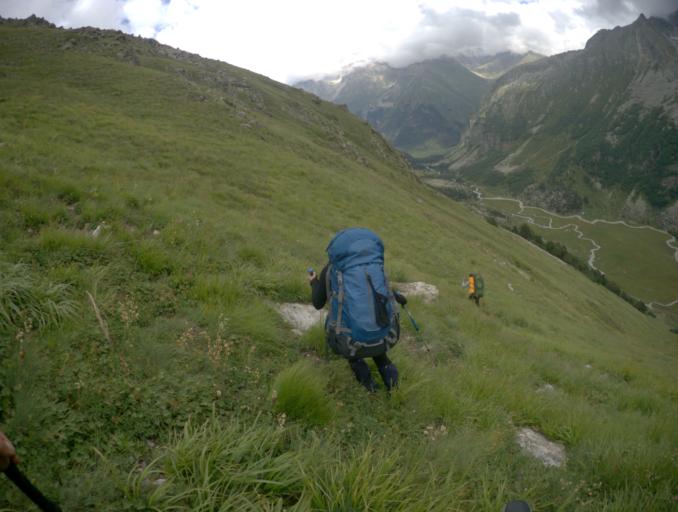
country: RU
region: Karachayevo-Cherkesiya
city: Uchkulan
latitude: 43.2689
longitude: 42.1359
